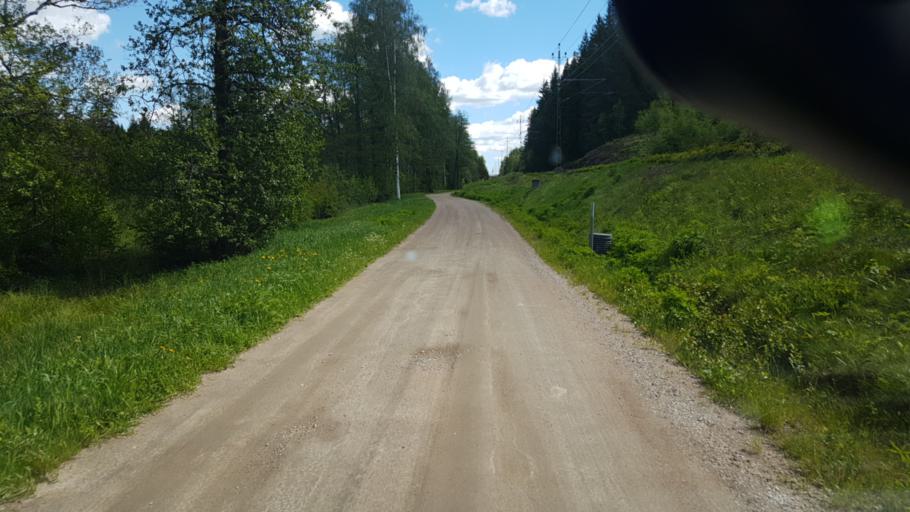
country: SE
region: Vaermland
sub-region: Karlstads Kommun
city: Edsvalla
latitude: 59.6132
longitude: 12.9775
